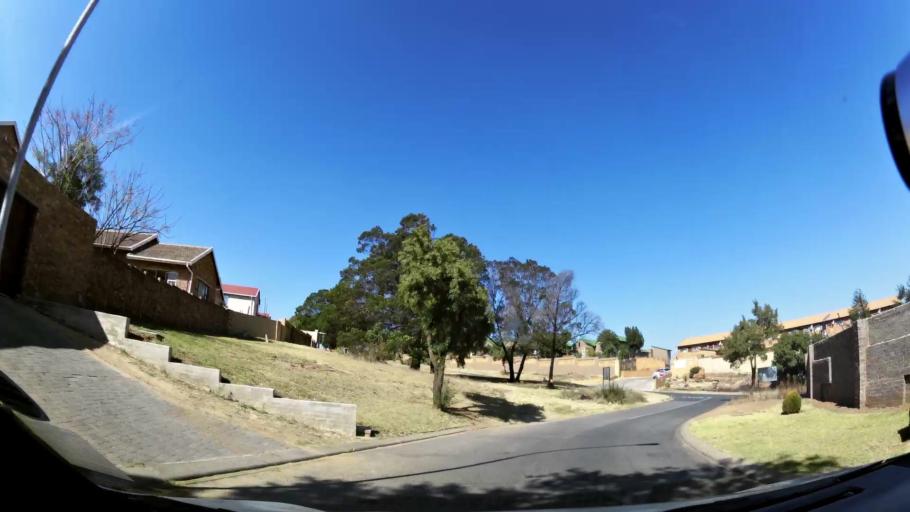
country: ZA
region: Gauteng
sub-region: City of Johannesburg Metropolitan Municipality
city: Johannesburg
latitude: -26.2659
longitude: 28.0194
